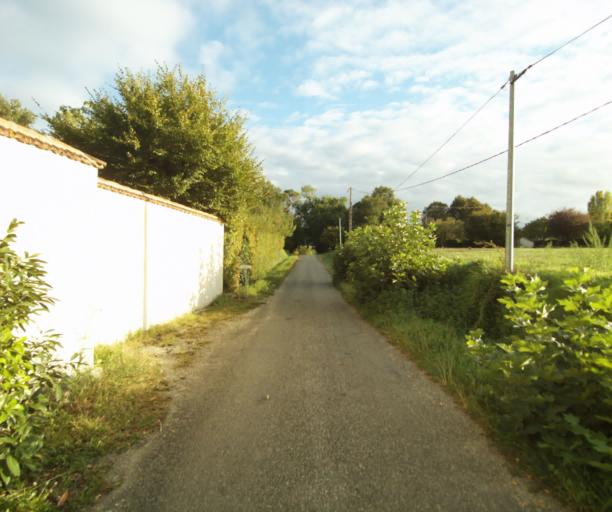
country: FR
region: Aquitaine
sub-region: Departement des Landes
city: Gabarret
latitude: 43.9515
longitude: 0.0749
